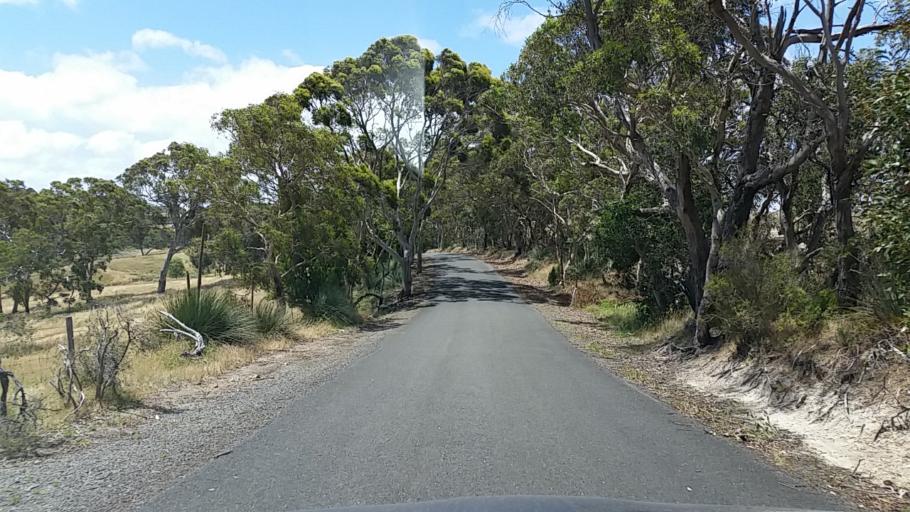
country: AU
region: South Australia
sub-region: Alexandrina
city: Mount Compass
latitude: -35.4461
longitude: 138.5922
